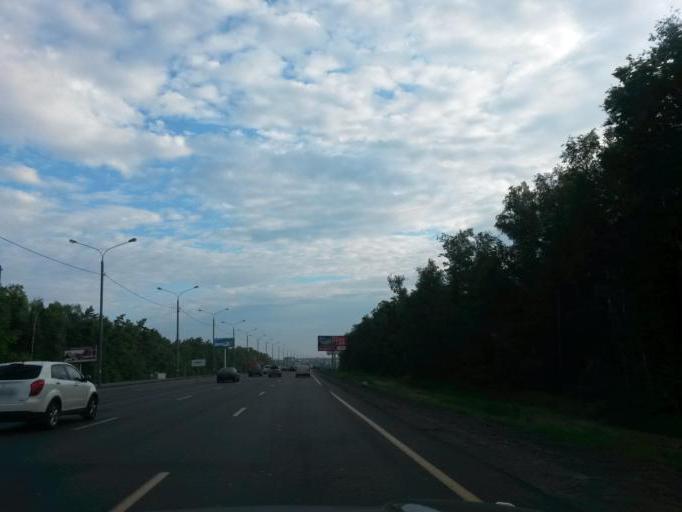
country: RU
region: Moskovskaya
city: Shcherbinka
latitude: 55.5144
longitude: 37.6089
